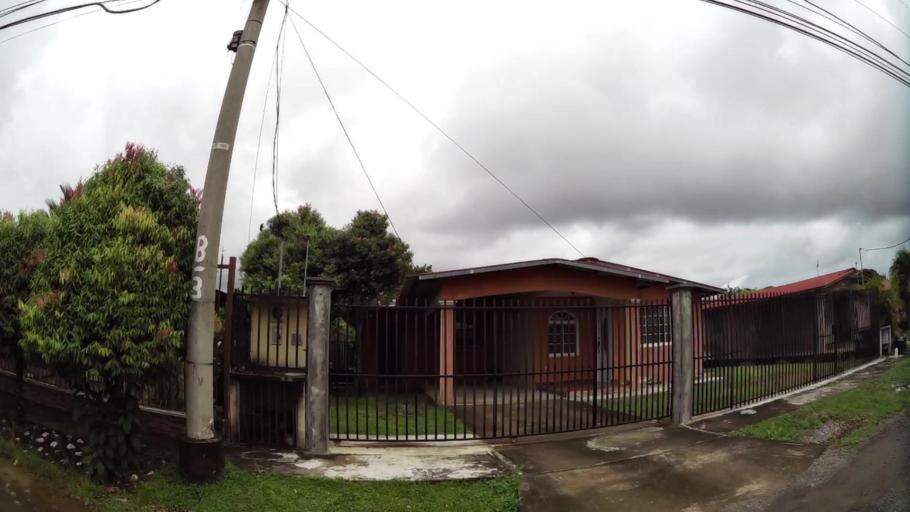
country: PA
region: Chiriqui
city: David
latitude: 8.4168
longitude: -82.4529
